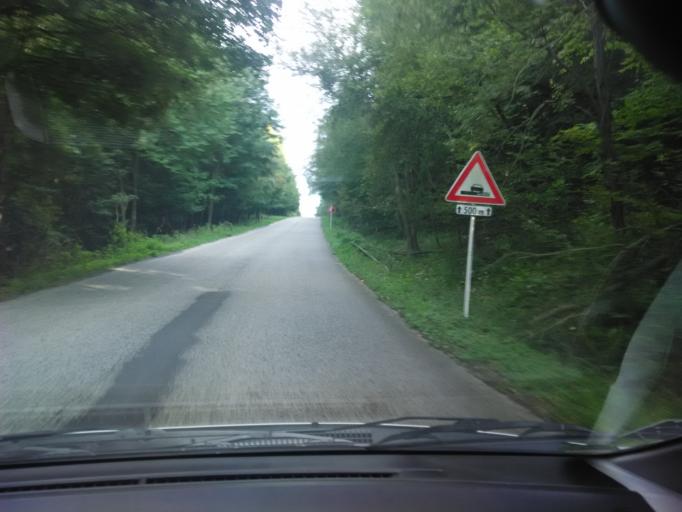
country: SK
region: Banskobystricky
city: Nova Bana
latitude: 48.3822
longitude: 18.7131
